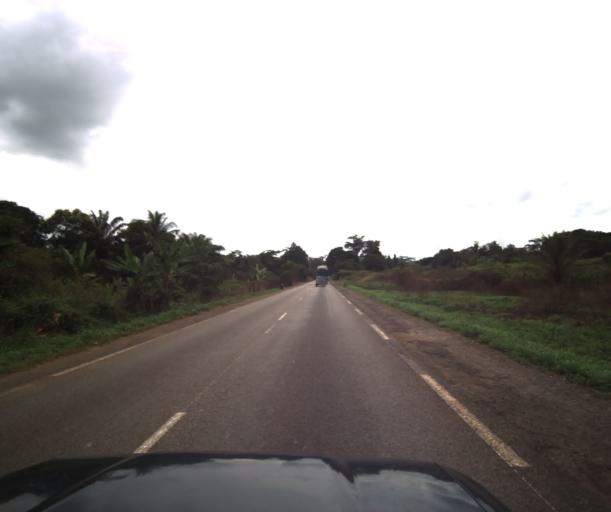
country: CM
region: Littoral
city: Edea
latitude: 3.8350
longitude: 10.4129
